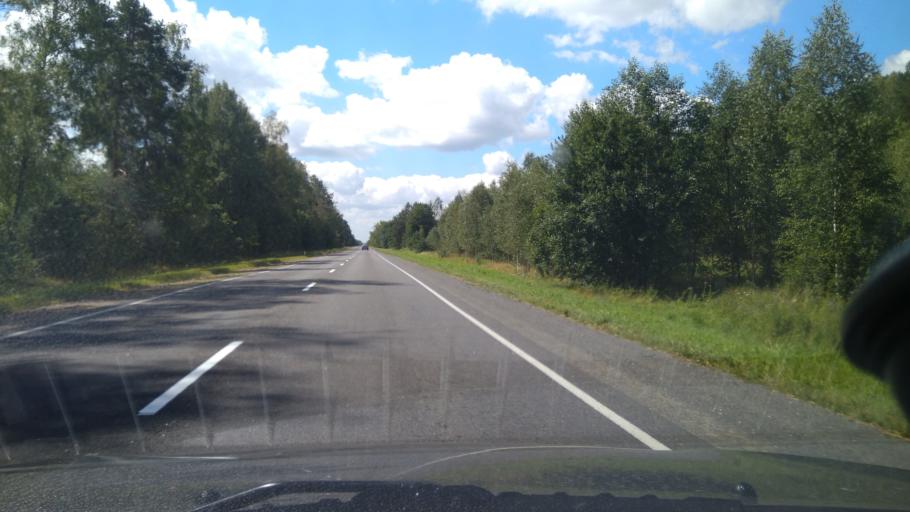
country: BY
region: Brest
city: Nyakhachava
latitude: 52.6611
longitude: 25.2400
